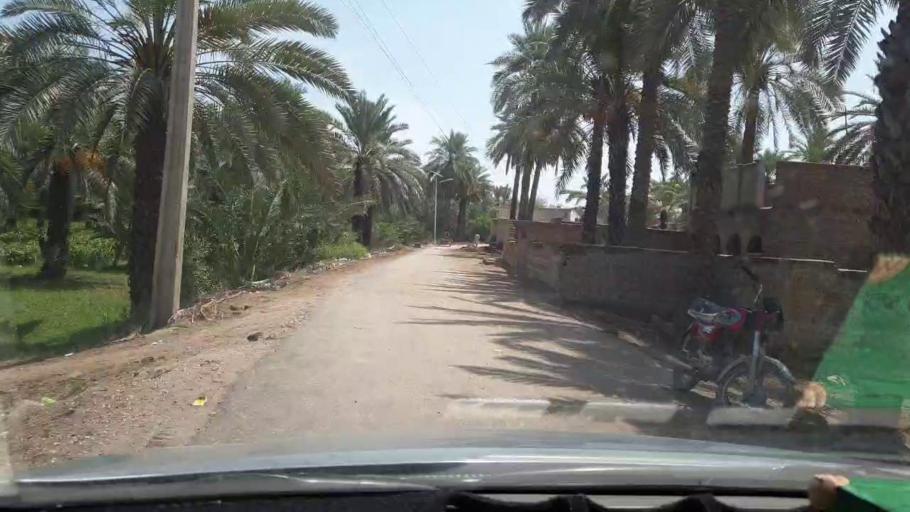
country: PK
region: Sindh
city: Khairpur
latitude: 27.4862
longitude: 68.7667
